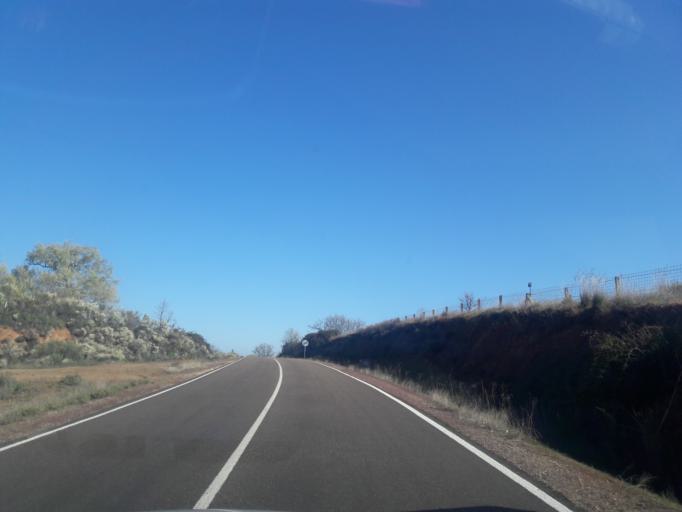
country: ES
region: Castille and Leon
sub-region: Provincia de Salamanca
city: Cabeza del Caballo
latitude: 41.1066
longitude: -6.5543
